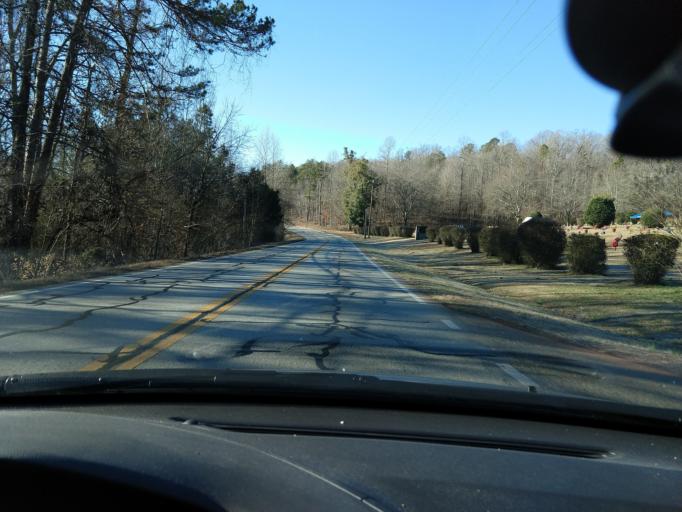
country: US
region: Georgia
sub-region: Jackson County
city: Commerce
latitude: 34.1788
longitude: -83.4859
